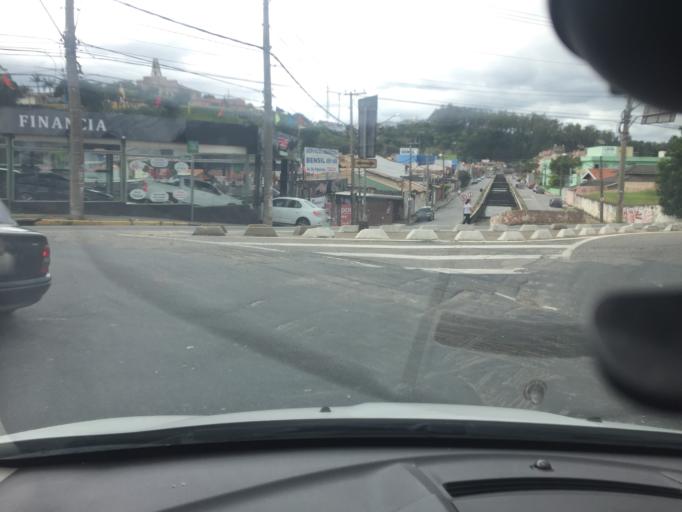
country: BR
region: Sao Paulo
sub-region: Varzea Paulista
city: Varzea Paulista
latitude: -23.2103
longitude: -46.8312
